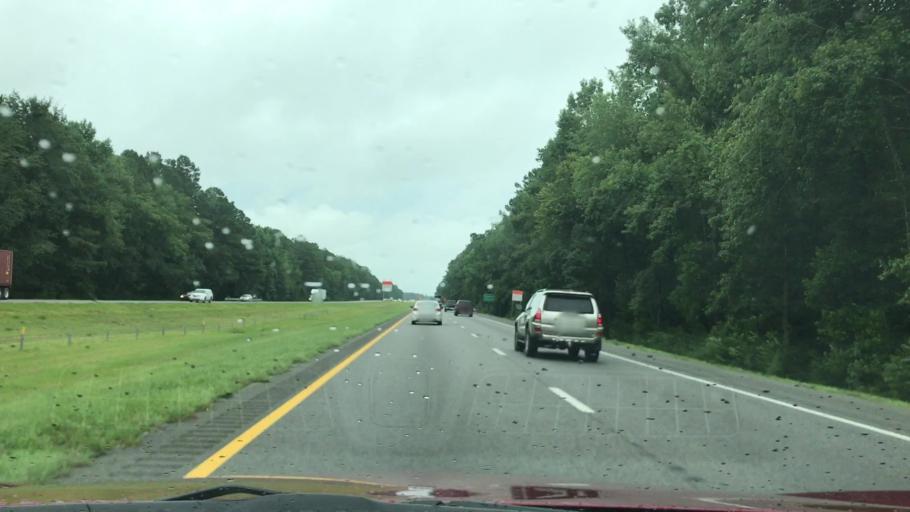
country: US
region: South Carolina
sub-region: Dorchester County
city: Ridgeville
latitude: 33.1319
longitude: -80.2999
